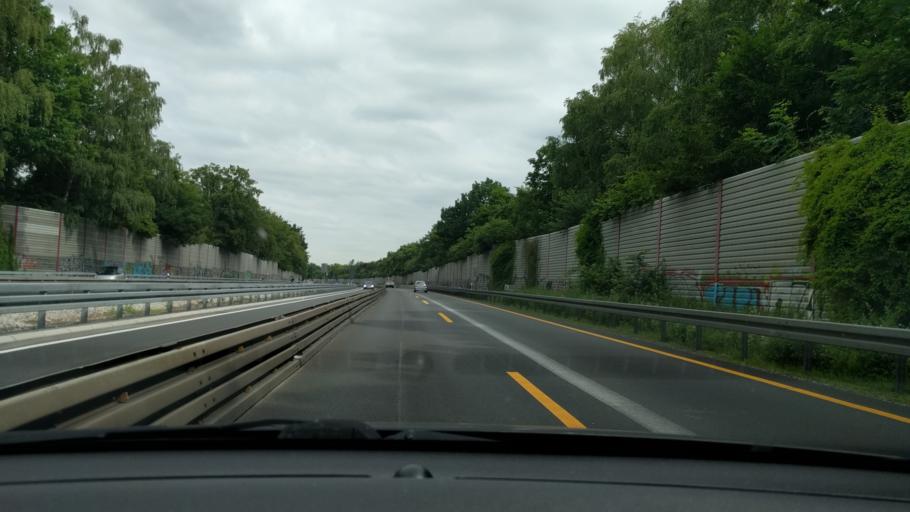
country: DE
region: North Rhine-Westphalia
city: Castrop-Rauxel
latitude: 51.5276
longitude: 7.3773
